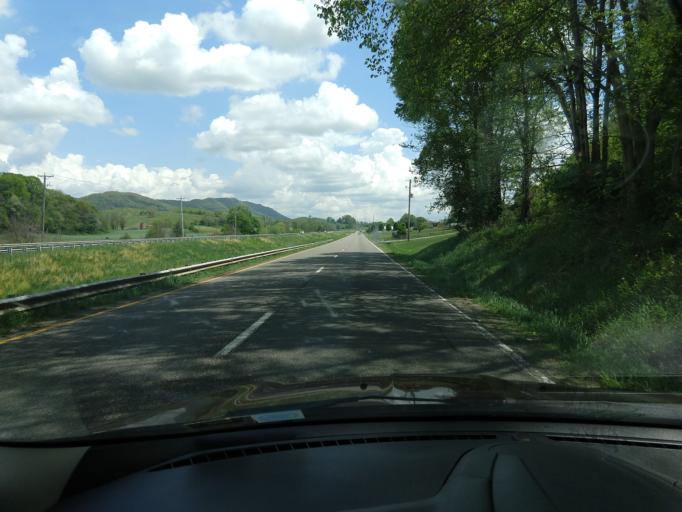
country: US
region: Virginia
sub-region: Russell County
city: Honaker
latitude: 36.9617
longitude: -81.9260
